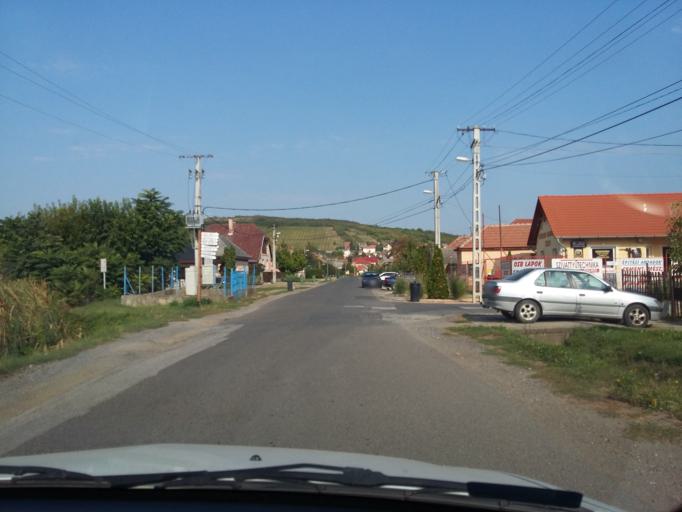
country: HU
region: Borsod-Abauj-Zemplen
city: Bekecs
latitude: 48.1483
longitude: 21.1790
